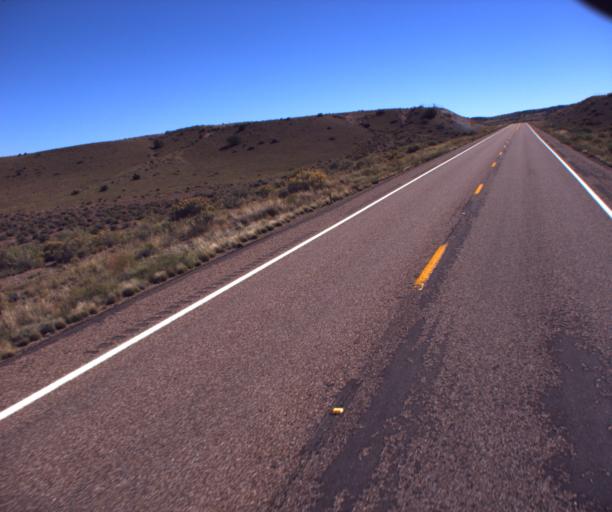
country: US
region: Arizona
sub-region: Apache County
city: Saint Johns
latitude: 34.5884
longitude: -109.5916
